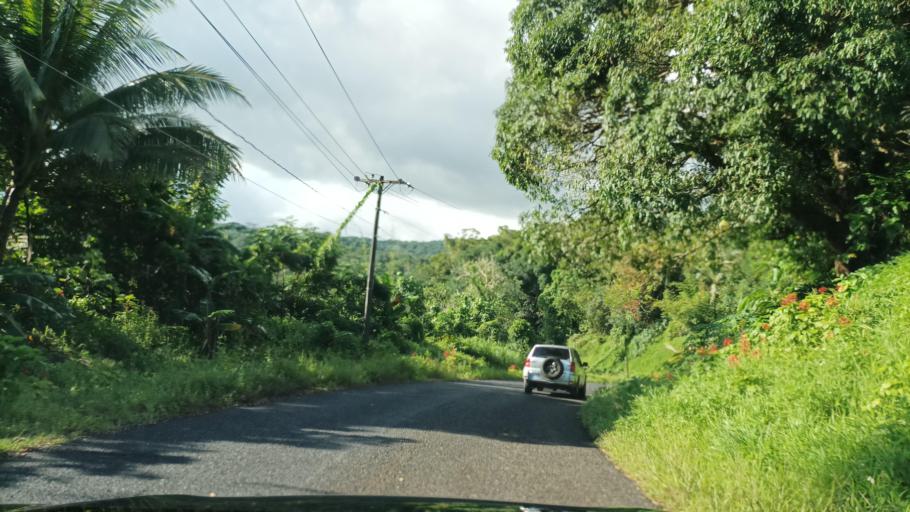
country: FM
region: Pohnpei
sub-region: Sokehs Municipality
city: Palikir - National Government Center
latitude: 6.8223
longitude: 158.1733
